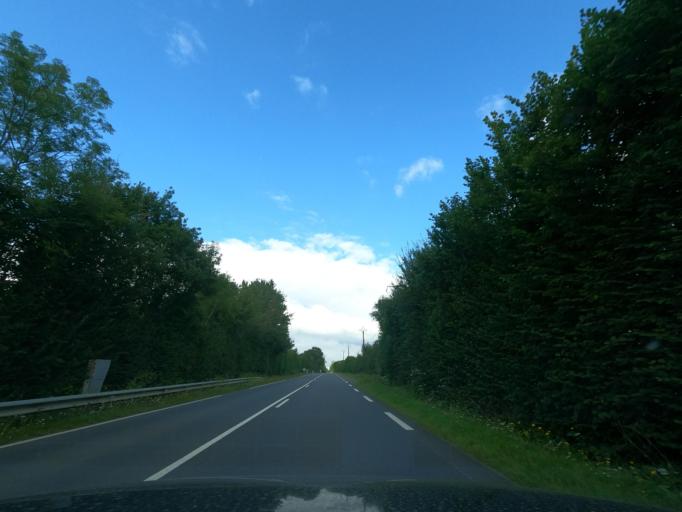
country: FR
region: Lower Normandy
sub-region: Departement de l'Orne
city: Gace
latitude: 48.8164
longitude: 0.3151
